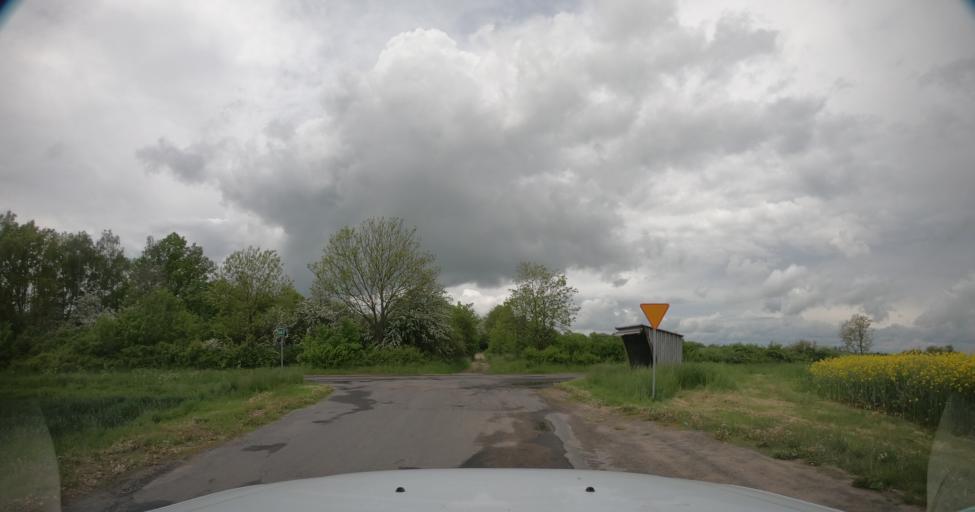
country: PL
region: West Pomeranian Voivodeship
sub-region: Powiat pyrzycki
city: Kozielice
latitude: 53.0819
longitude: 14.8296
